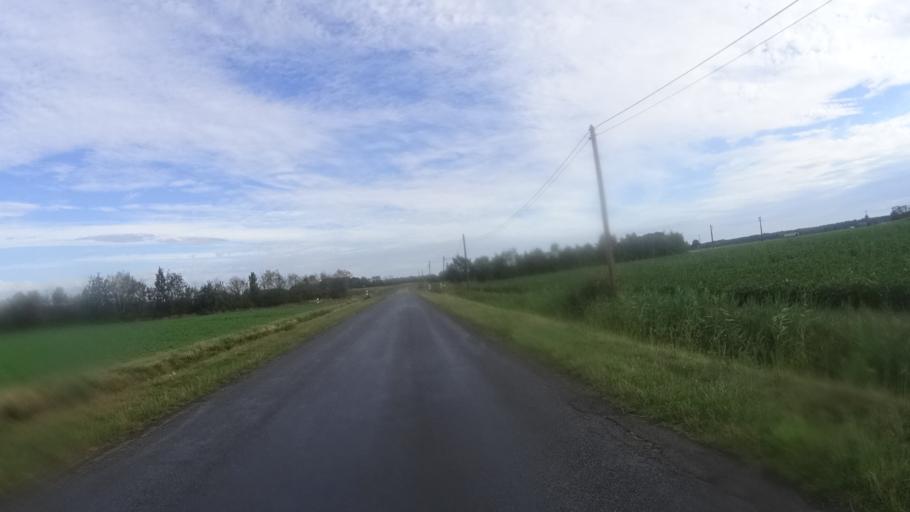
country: FR
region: Centre
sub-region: Departement du Loiret
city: Chateauneuf-sur-Loire
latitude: 47.8857
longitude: 2.2128
